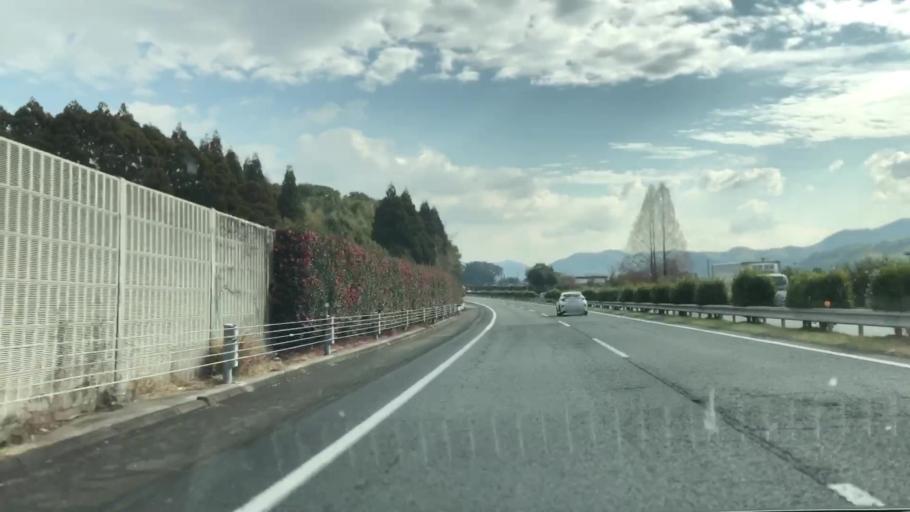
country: JP
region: Fukuoka
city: Setakamachi-takayanagi
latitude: 33.1233
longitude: 130.5195
